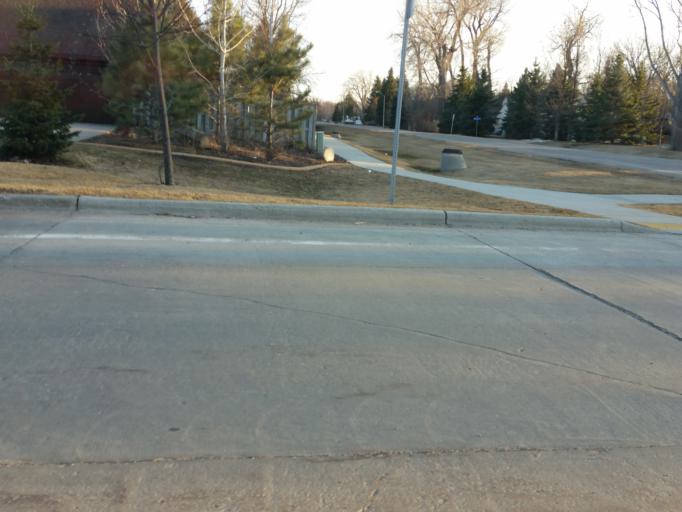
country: US
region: North Dakota
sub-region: Grand Forks County
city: Grand Forks
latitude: 47.8750
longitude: -97.0290
